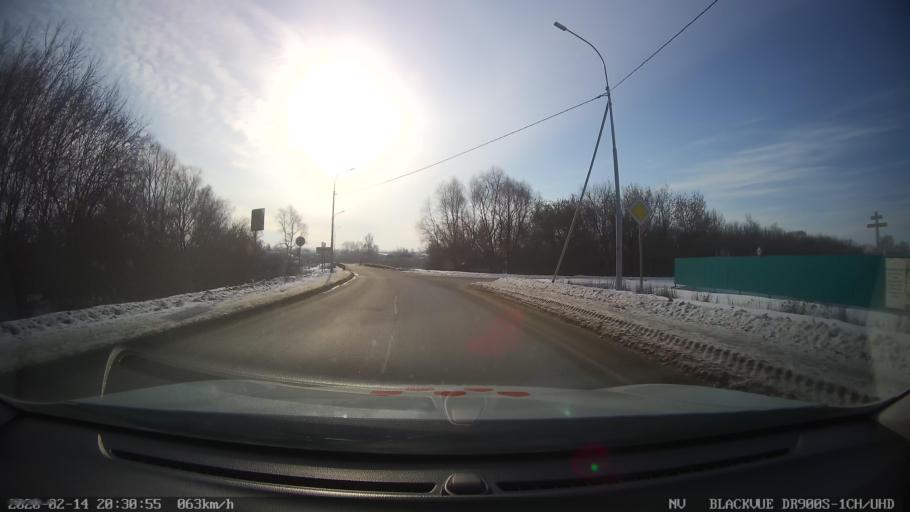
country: RU
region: Tatarstan
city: Stolbishchi
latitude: 55.4391
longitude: 48.9920
